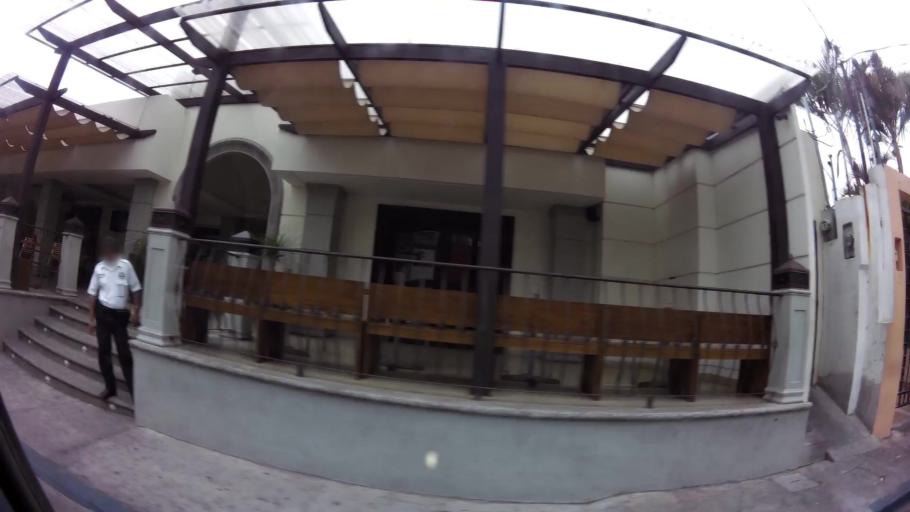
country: HN
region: Francisco Morazan
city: Tegucigalpa
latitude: 14.1004
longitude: -87.1963
